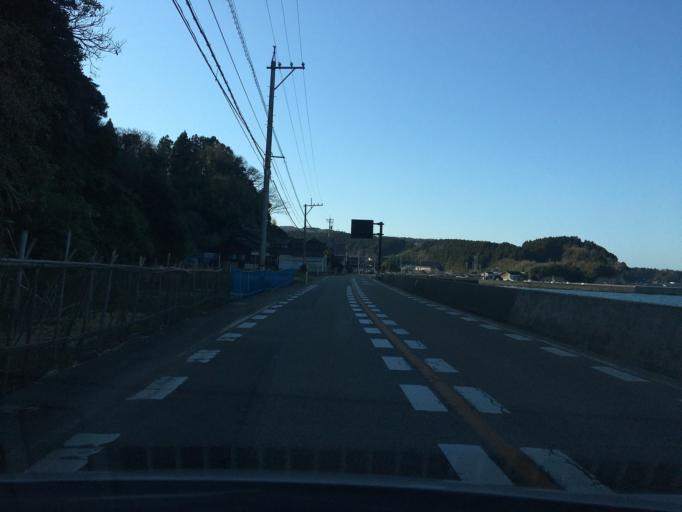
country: JP
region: Ishikawa
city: Nanao
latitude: 36.9740
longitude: 137.0516
